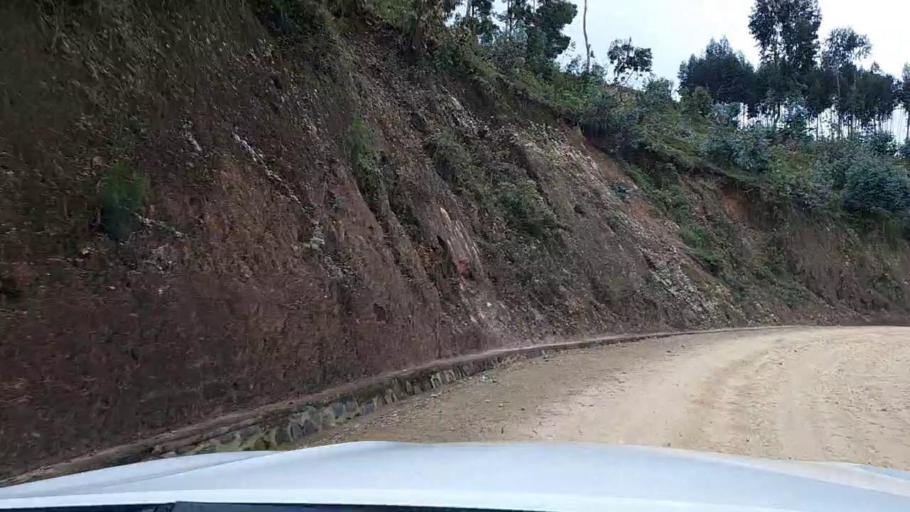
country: RW
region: Southern Province
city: Nzega
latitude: -2.3796
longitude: 29.3830
